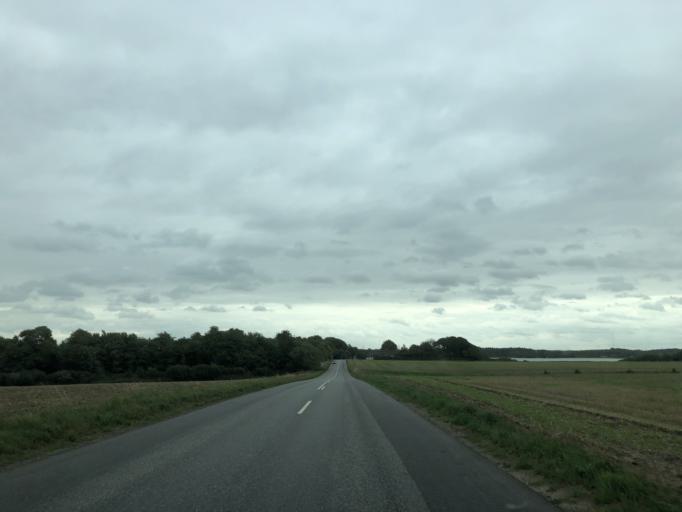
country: DK
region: Central Jutland
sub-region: Herning Kommune
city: Snejbjerg
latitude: 56.1623
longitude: 8.8931
